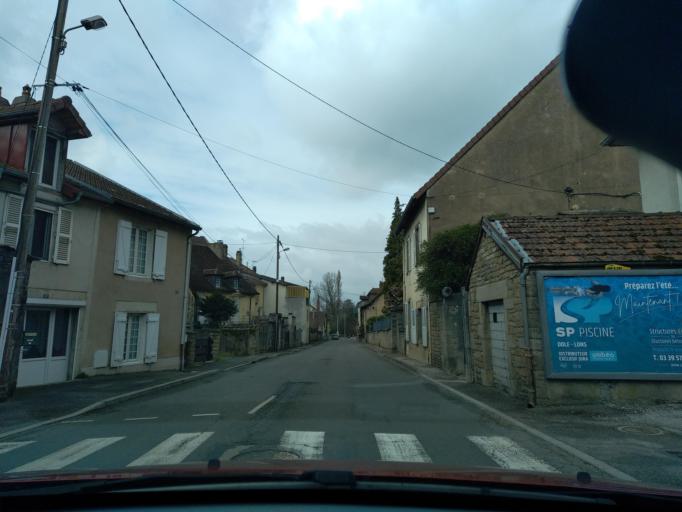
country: FR
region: Franche-Comte
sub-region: Departement du Jura
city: Perrigny
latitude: 46.6554
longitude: 5.5969
